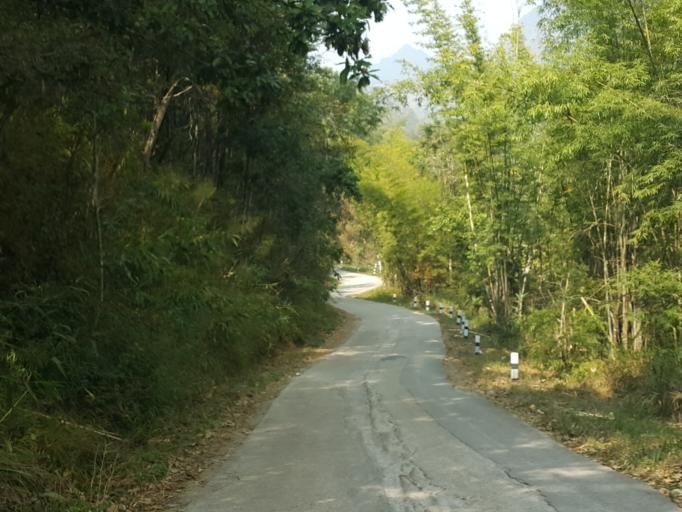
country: TH
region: Chiang Mai
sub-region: Amphoe Chiang Dao
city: Chiang Dao
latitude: 19.4118
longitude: 98.8552
